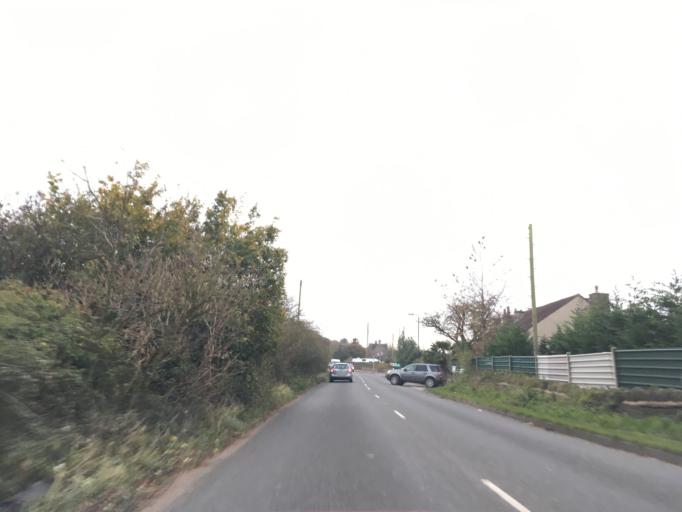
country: GB
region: England
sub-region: South Gloucestershire
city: Yate
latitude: 51.5232
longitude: -2.4348
